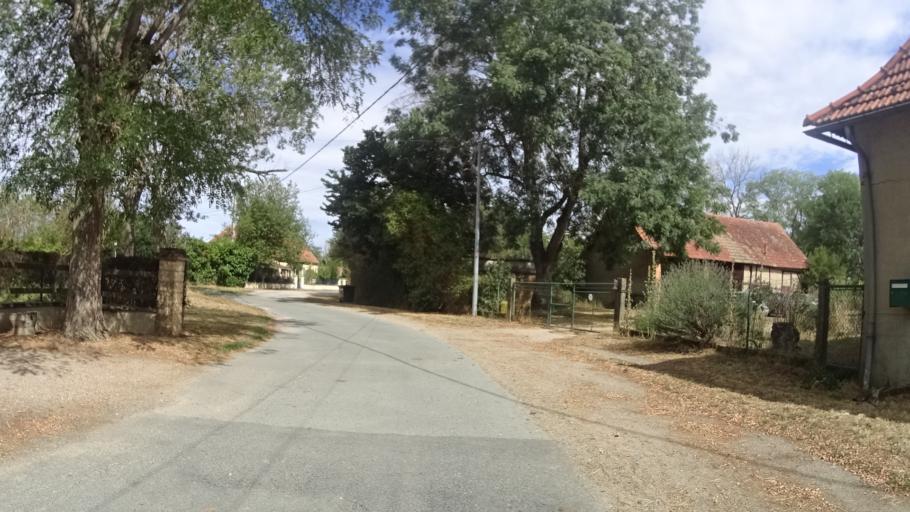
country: FR
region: Auvergne
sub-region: Departement de l'Allier
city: Beaulon
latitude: 46.6502
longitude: 3.6876
